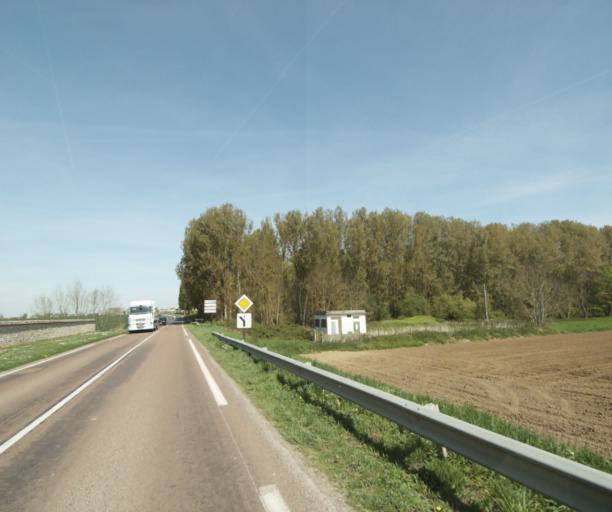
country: FR
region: Ile-de-France
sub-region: Departement de Seine-et-Marne
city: Nangis
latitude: 48.5431
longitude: 3.0174
